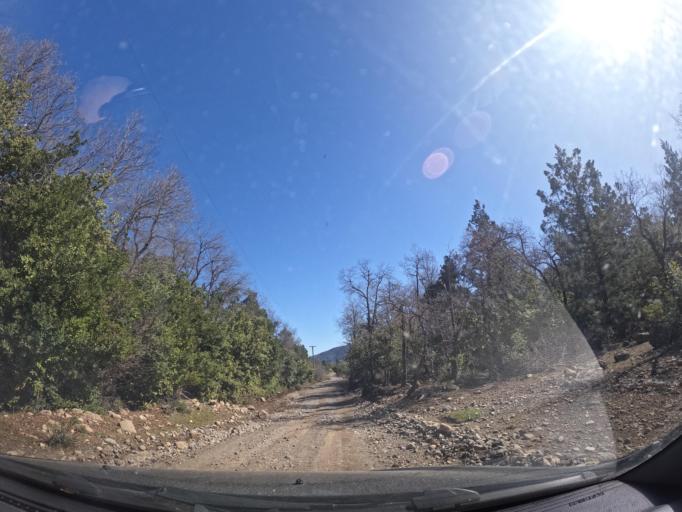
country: CL
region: Maule
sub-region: Provincia de Linares
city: Longavi
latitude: -36.2445
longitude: -71.3440
